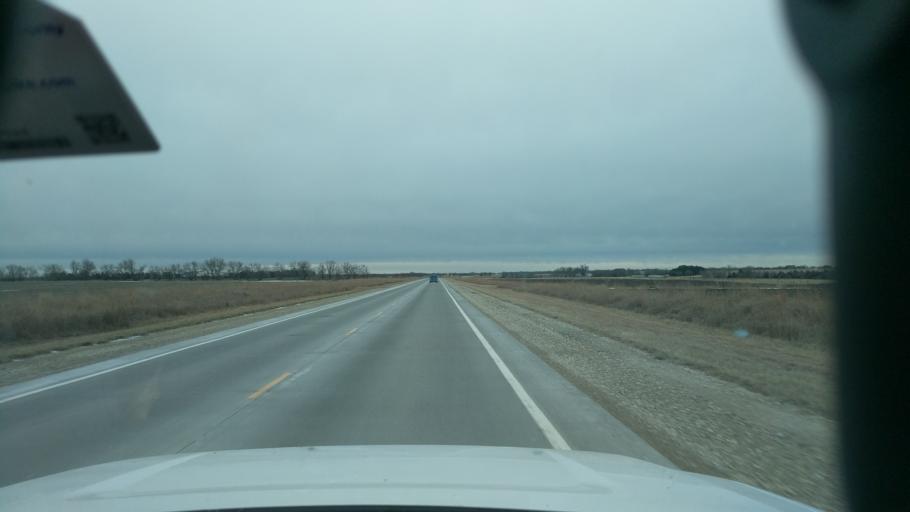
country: US
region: Kansas
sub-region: Dickinson County
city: Herington
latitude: 38.5326
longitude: -96.9567
